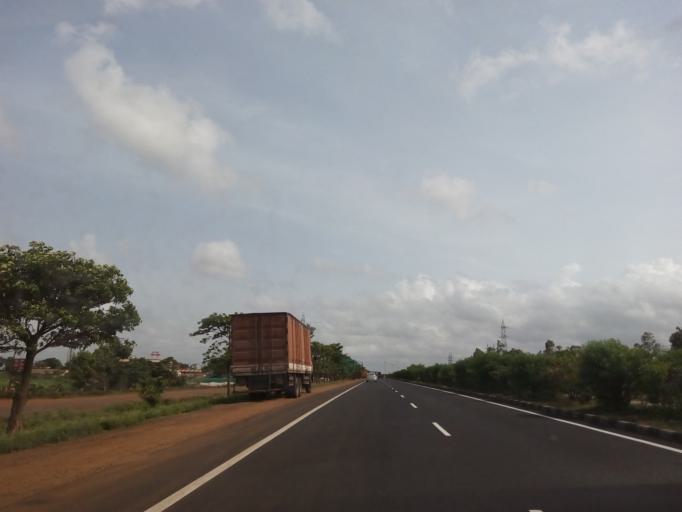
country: IN
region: Karnataka
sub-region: Belgaum
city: Sankeshwar
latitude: 16.1519
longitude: 74.5177
